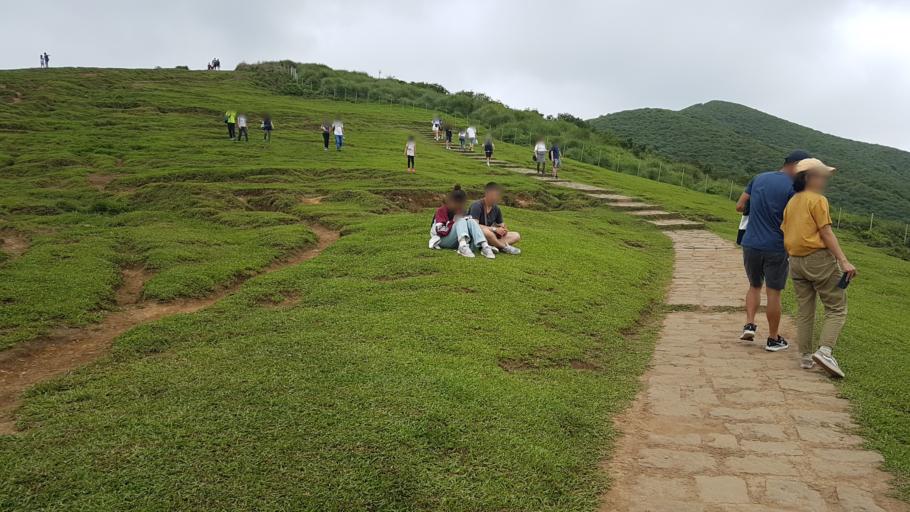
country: TW
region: Taipei
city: Taipei
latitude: 25.1622
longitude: 121.5744
